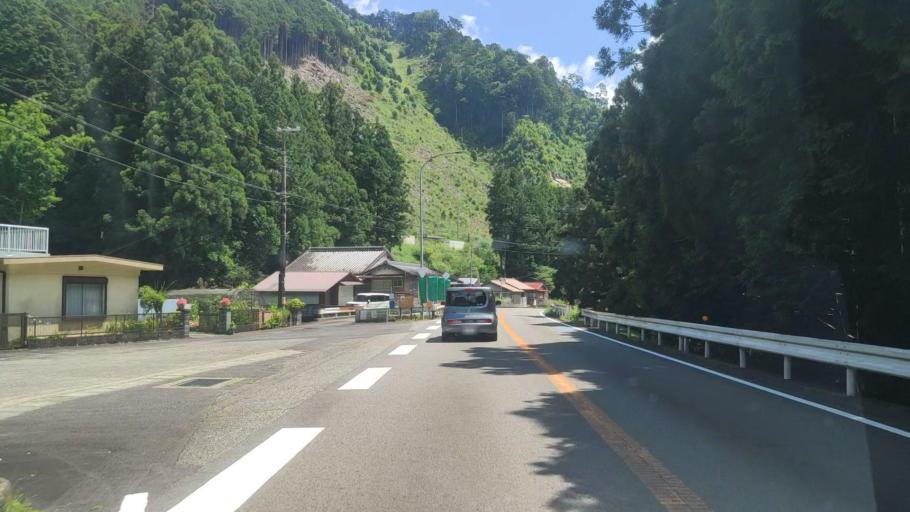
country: JP
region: Mie
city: Owase
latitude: 33.9843
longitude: 136.1083
